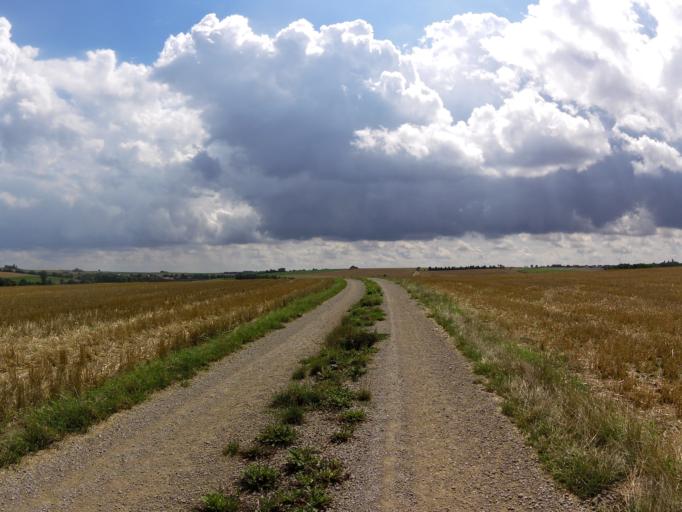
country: DE
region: Bavaria
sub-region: Regierungsbezirk Unterfranken
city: Reichenberg
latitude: 49.7192
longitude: 9.9123
